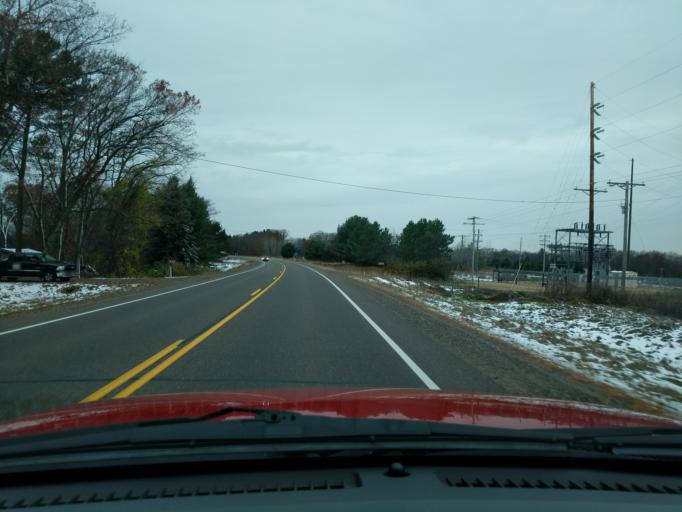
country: US
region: Wisconsin
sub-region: Burnett County
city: Siren
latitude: 45.8232
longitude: -92.2513
